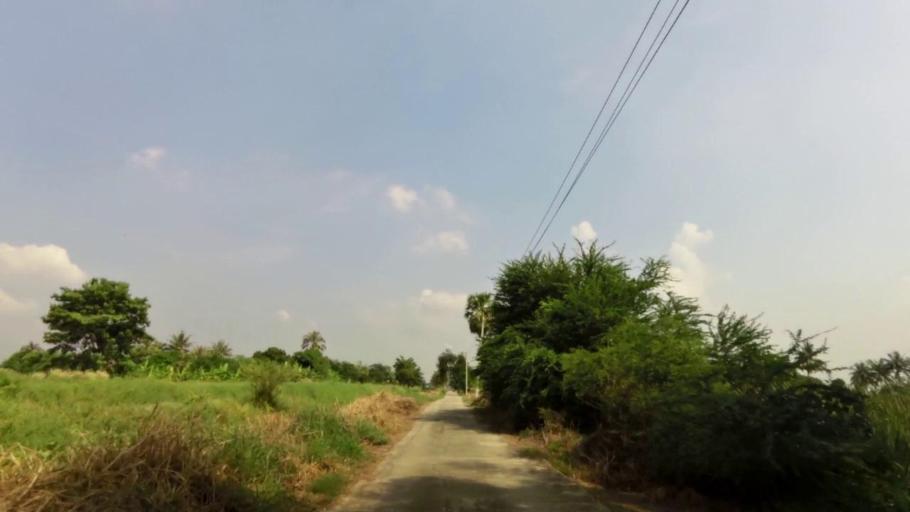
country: TH
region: Ang Thong
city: Wiset Chaichan
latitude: 14.6113
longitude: 100.3937
